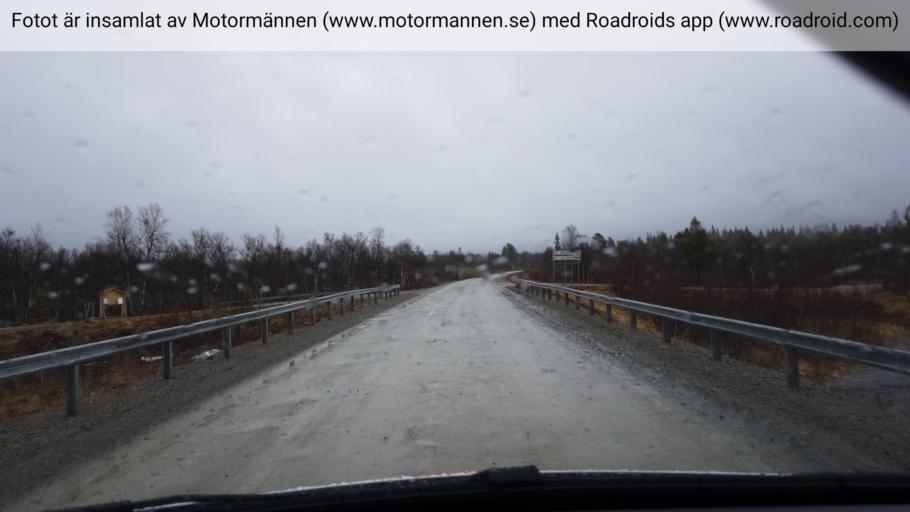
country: SE
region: Jaemtland
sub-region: Are Kommun
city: Are
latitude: 62.6680
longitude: 12.9103
